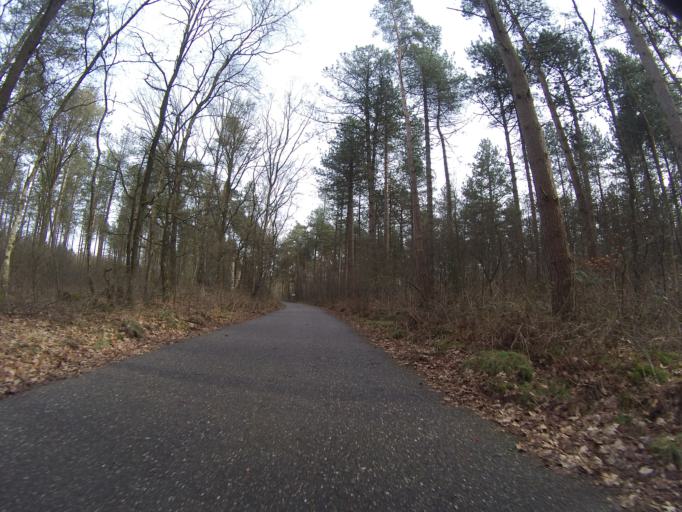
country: NL
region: Utrecht
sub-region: Gemeente Utrechtse Heuvelrug
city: Maarn
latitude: 52.0966
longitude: 5.3335
